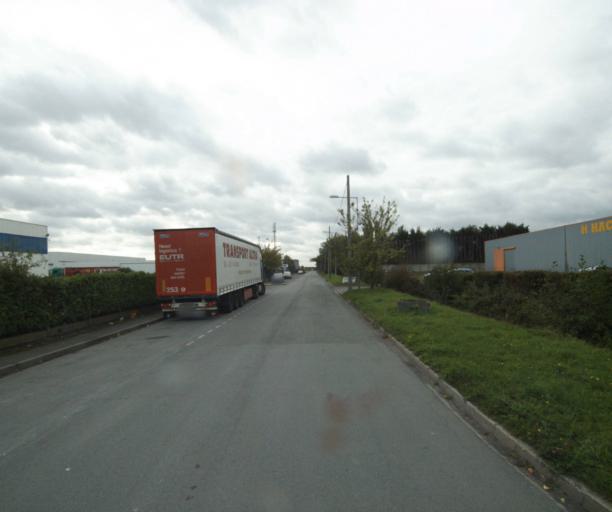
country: FR
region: Nord-Pas-de-Calais
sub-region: Departement du Nord
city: Bois-Grenier
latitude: 50.6503
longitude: 2.9049
